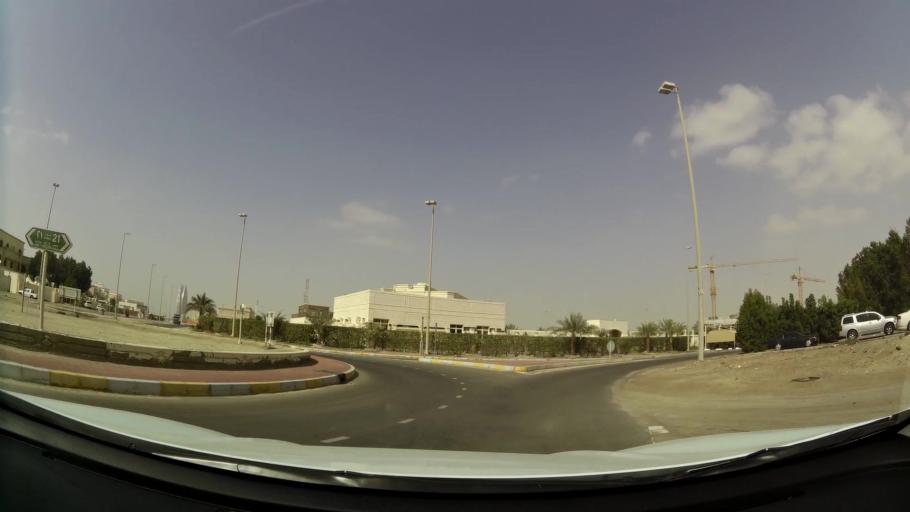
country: AE
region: Abu Dhabi
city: Abu Dhabi
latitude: 24.4288
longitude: 54.5809
